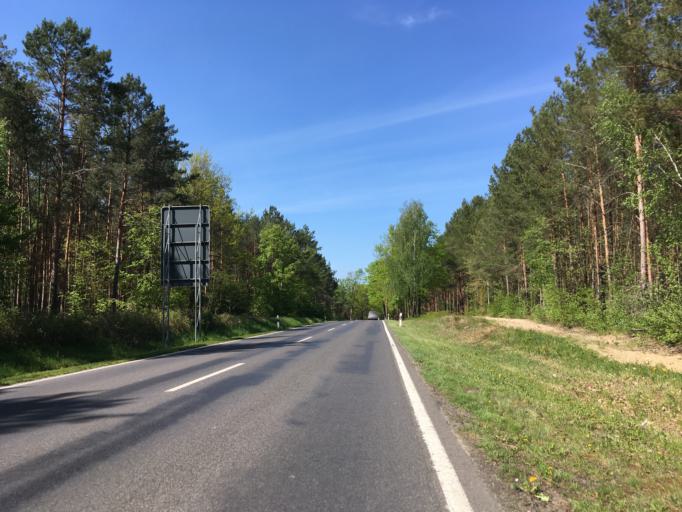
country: DE
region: Brandenburg
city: Marienwerder
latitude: 52.7759
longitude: 13.5608
